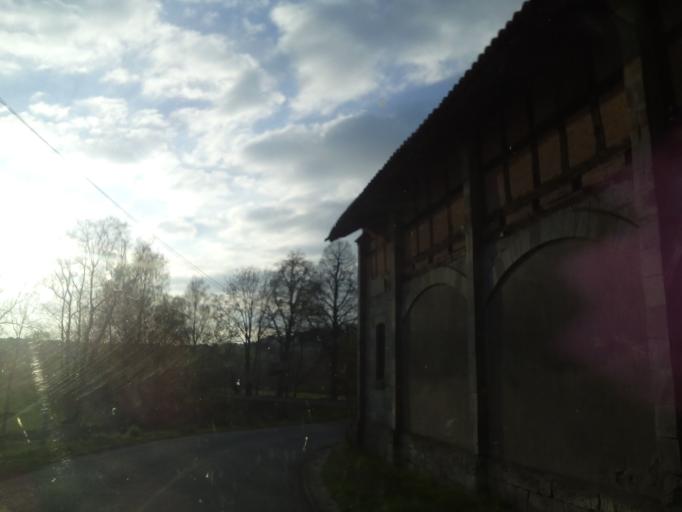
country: DE
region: Bavaria
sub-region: Regierungsbezirk Unterfranken
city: Maroldsweisach
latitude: 50.1831
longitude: 10.6995
